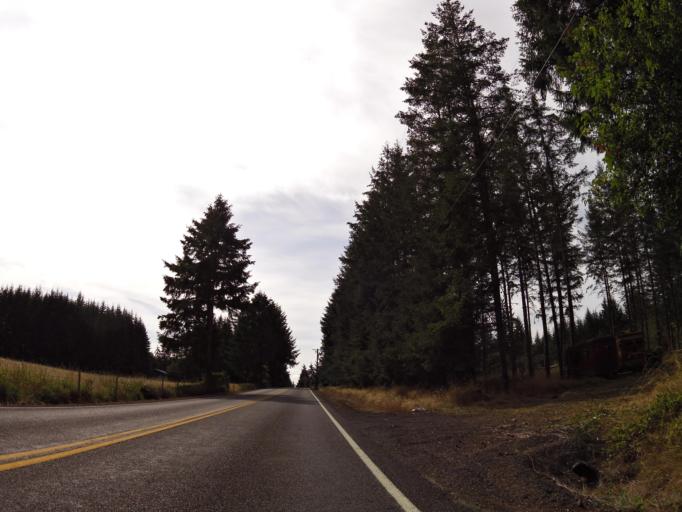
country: US
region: Washington
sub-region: Lewis County
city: Chehalis
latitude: 46.6030
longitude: -122.9712
